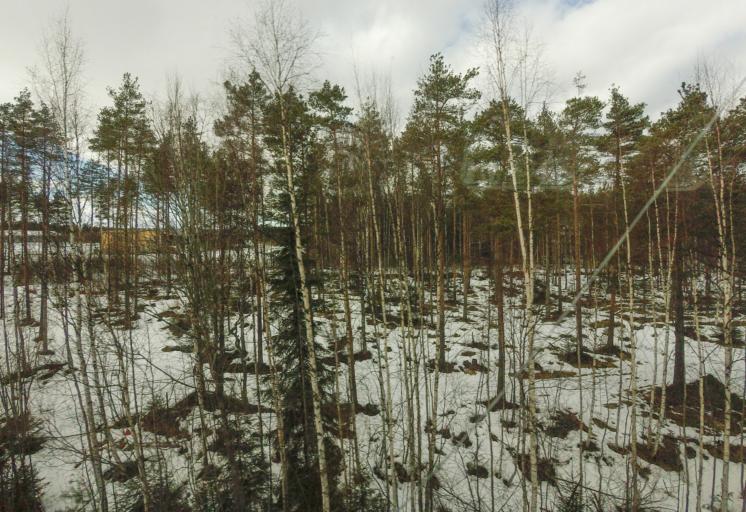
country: FI
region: South Karelia
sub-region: Imatra
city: Ruokolahti
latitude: 61.2948
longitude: 29.0635
